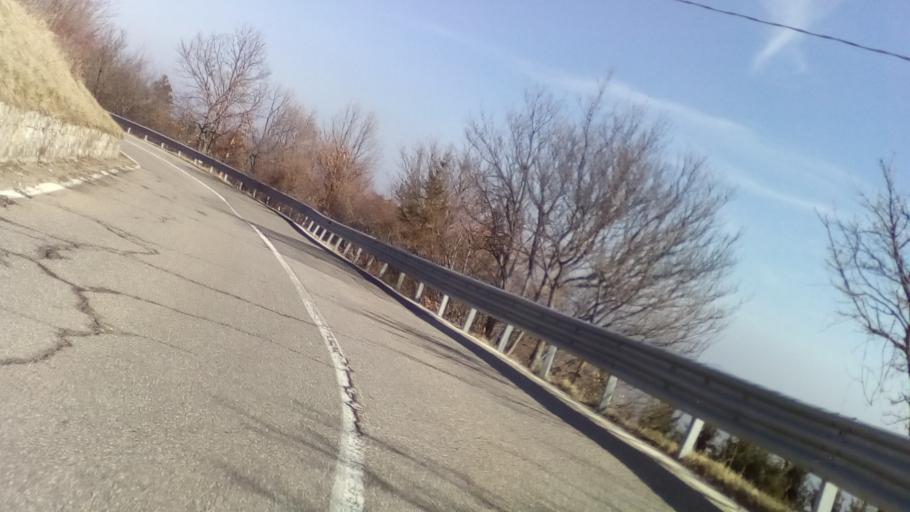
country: IT
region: Emilia-Romagna
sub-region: Provincia di Modena
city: Lama
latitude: 44.2872
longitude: 10.7066
